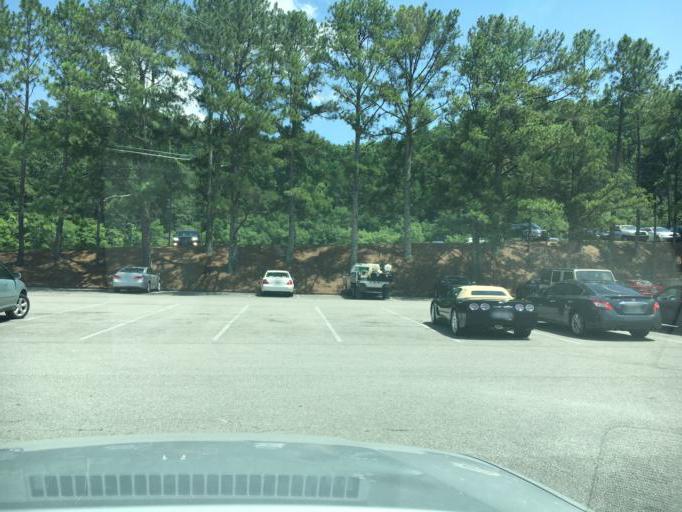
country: US
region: Alabama
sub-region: Jefferson County
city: Vestavia Hills
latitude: 33.4719
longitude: -86.7685
